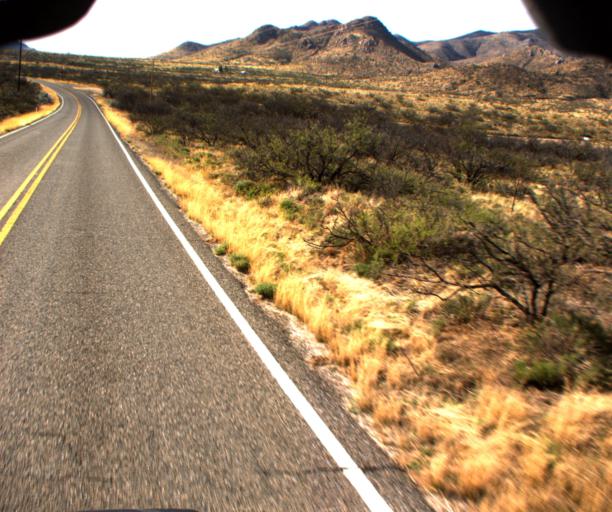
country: US
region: Arizona
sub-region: Cochise County
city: Willcox
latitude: 32.1731
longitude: -109.6021
